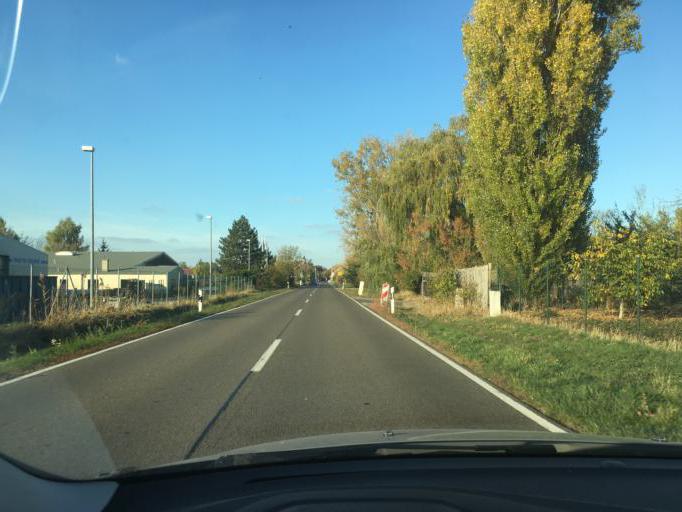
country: DE
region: Saxony-Anhalt
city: Lutzen
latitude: 51.2465
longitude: 12.1391
